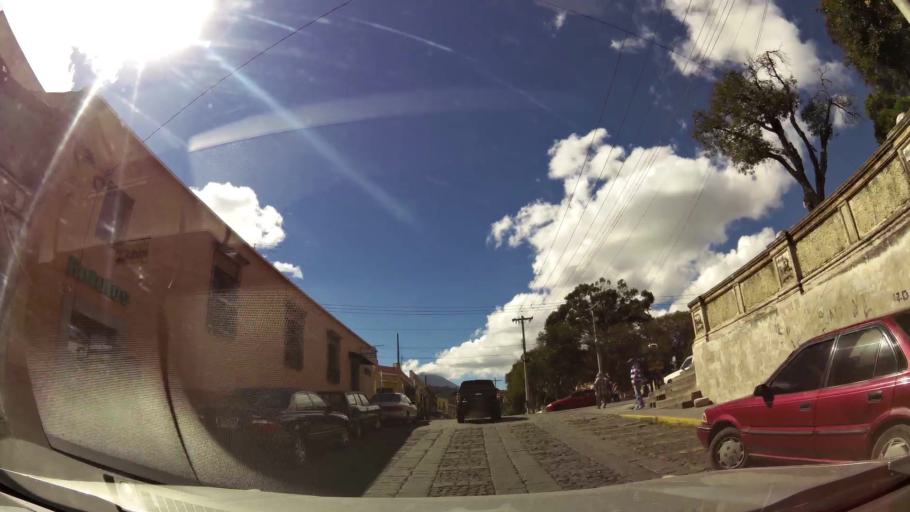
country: GT
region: Quetzaltenango
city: Quetzaltenango
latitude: 14.8399
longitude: -91.5162
